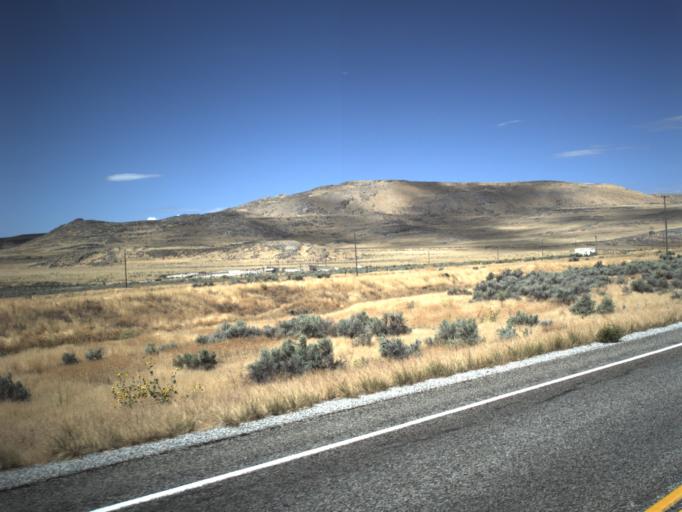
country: US
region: Utah
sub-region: Box Elder County
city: Tremonton
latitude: 41.6557
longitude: -112.4403
